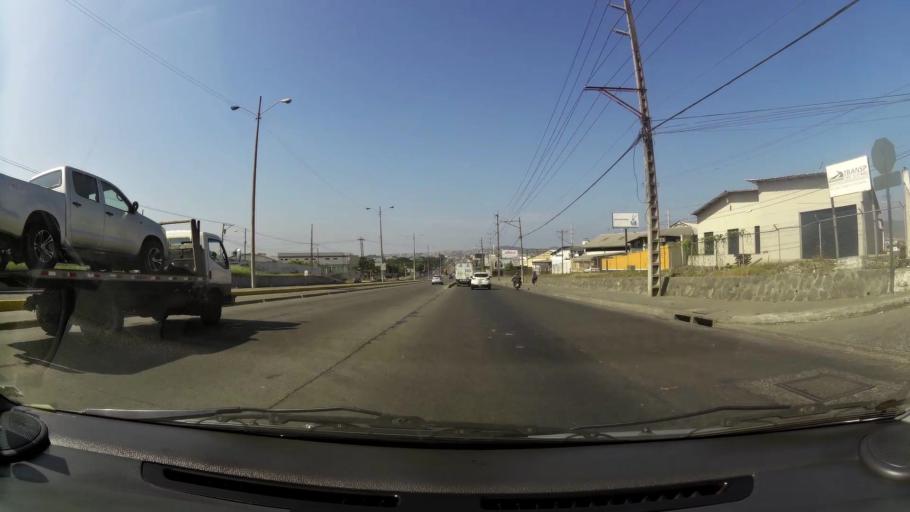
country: EC
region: Guayas
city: Santa Lucia
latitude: -2.1095
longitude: -79.9341
